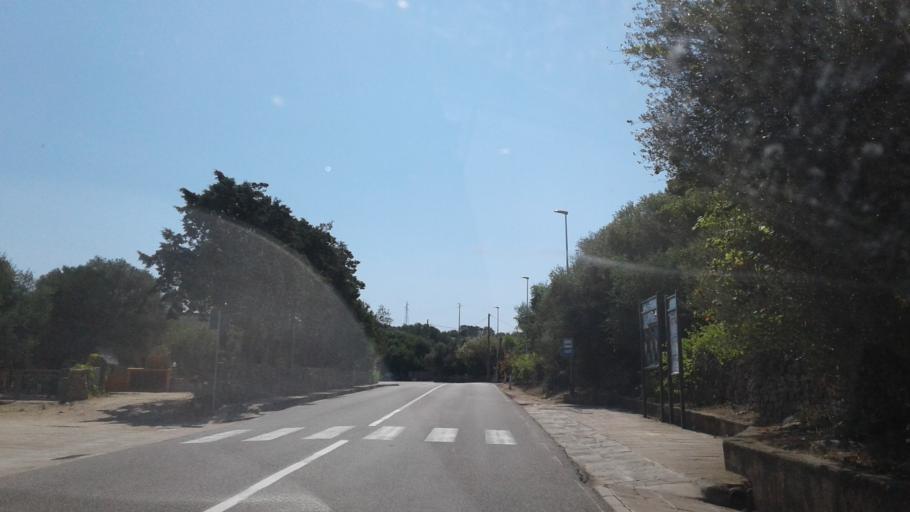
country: IT
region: Sardinia
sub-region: Provincia di Olbia-Tempio
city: Palau
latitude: 41.1703
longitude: 9.3214
